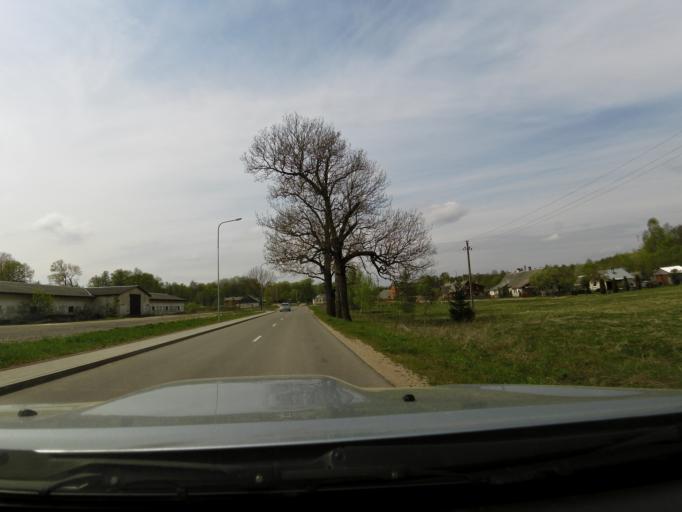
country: LT
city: Salcininkai
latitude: 54.4324
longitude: 25.3049
